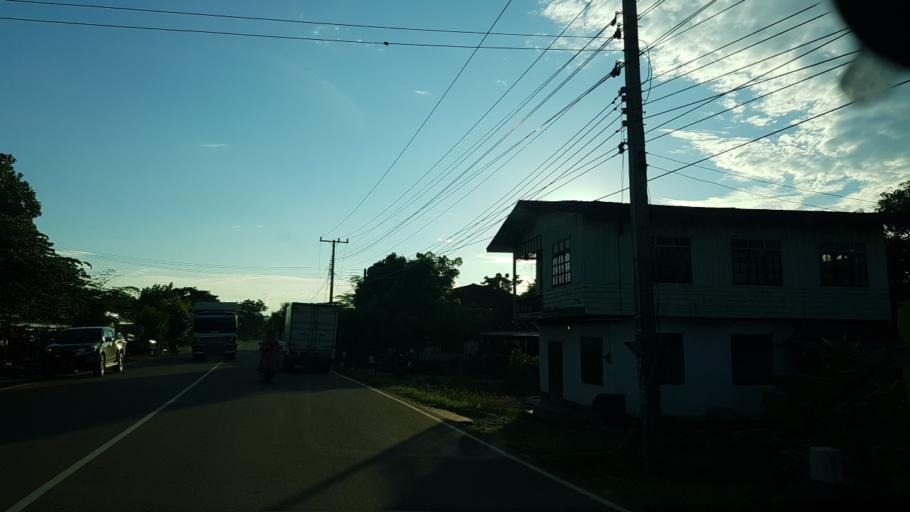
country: TH
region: Nong Khai
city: Sangkhom
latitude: 18.0558
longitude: 102.3140
